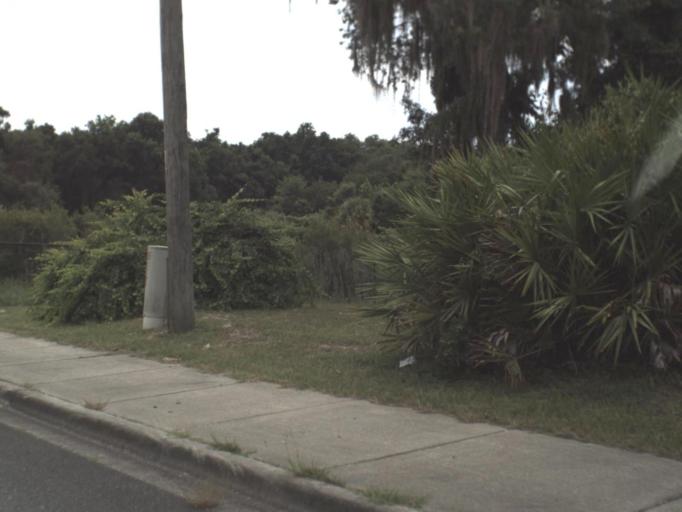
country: US
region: Florida
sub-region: Citrus County
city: Inverness
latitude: 28.8408
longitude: -82.2938
